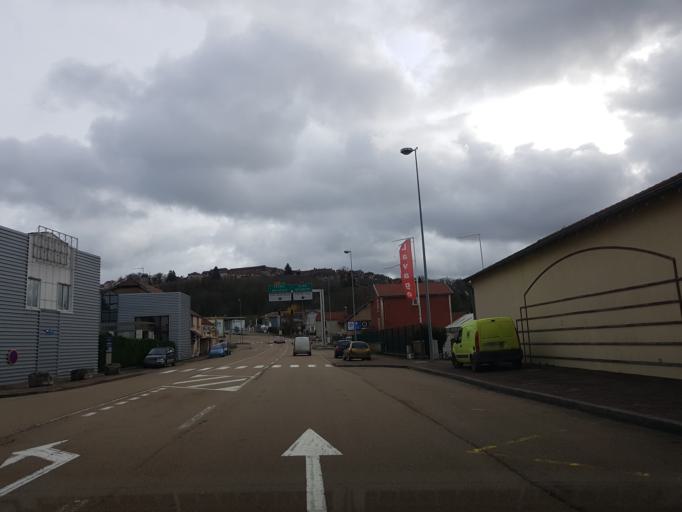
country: FR
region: Champagne-Ardenne
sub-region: Departement de la Haute-Marne
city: Langres
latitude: 47.8715
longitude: 5.3262
